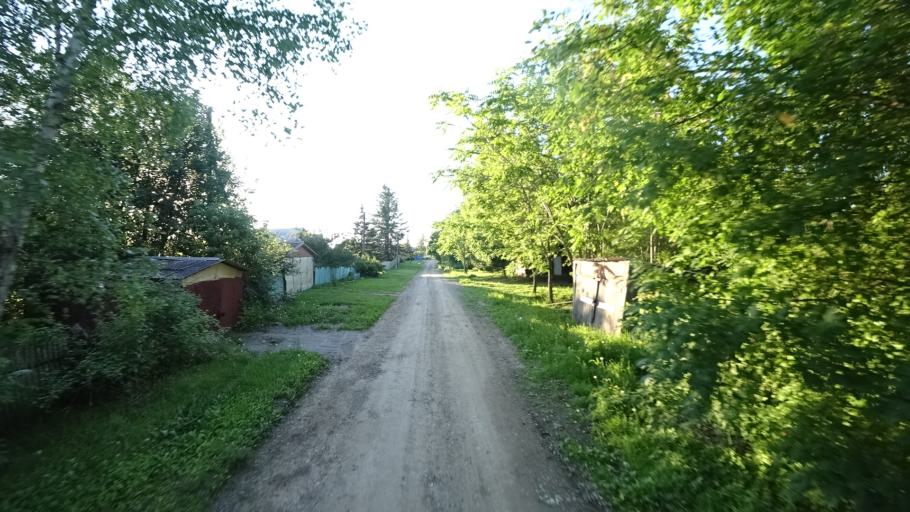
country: RU
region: Khabarovsk Krai
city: Khor
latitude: 47.8547
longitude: 135.0029
